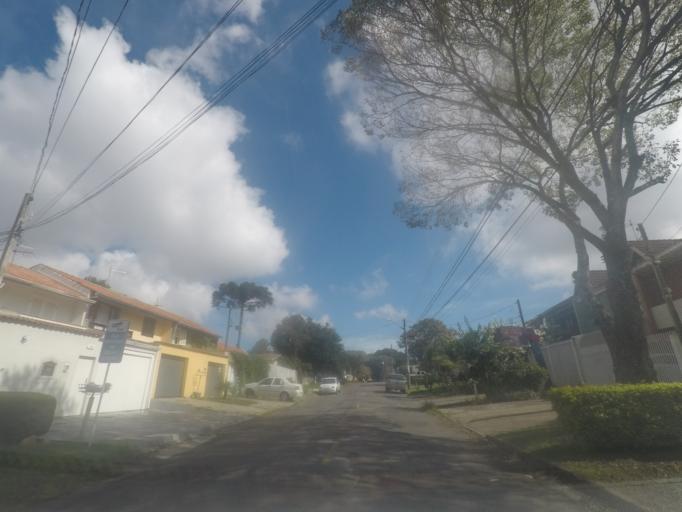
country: BR
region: Parana
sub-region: Pinhais
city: Pinhais
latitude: -25.4587
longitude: -49.2273
